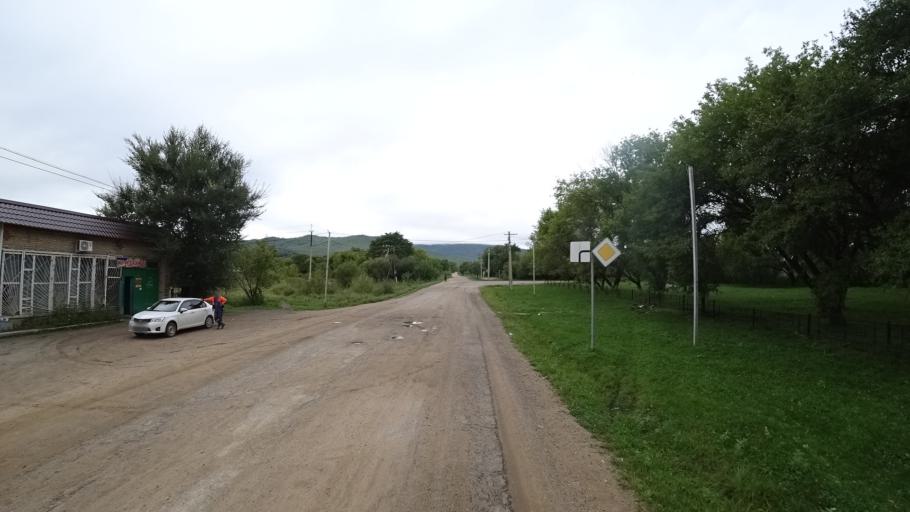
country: RU
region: Primorskiy
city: Rettikhovka
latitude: 44.1382
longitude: 132.6469
